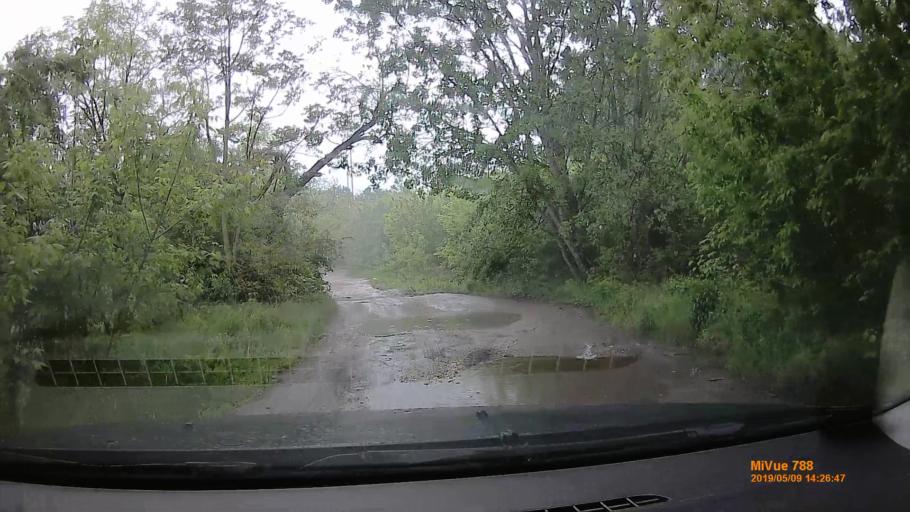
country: HU
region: Budapest
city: Budapest XVII. keruelet
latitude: 47.4935
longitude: 19.2200
